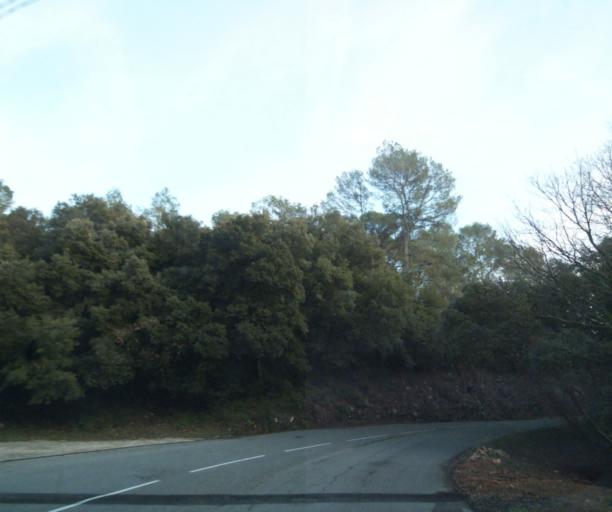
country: FR
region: Provence-Alpes-Cote d'Azur
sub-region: Departement du Var
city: Trans-en-Provence
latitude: 43.5002
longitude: 6.4966
